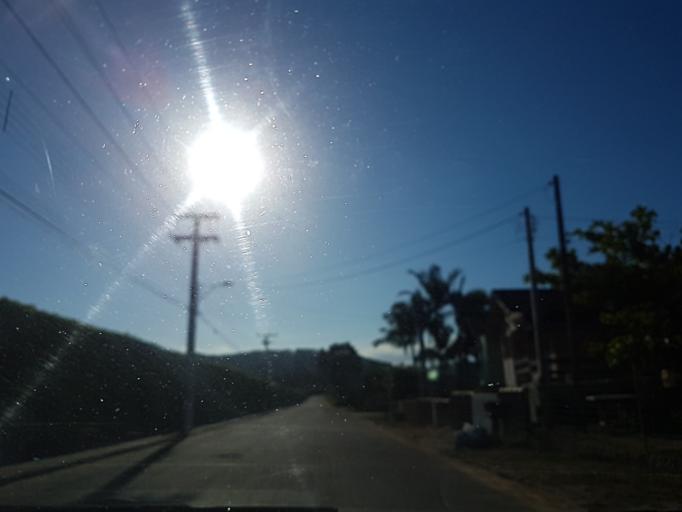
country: BR
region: Santa Catarina
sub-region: Braco Do Norte
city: Braco do Norte
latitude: -28.3301
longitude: -49.1679
